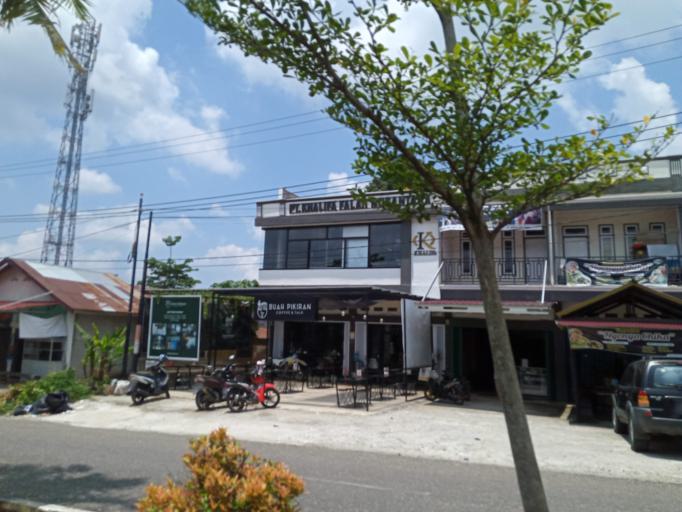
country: ID
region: Jambi
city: Bangko
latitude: -2.0582
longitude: 102.2780
